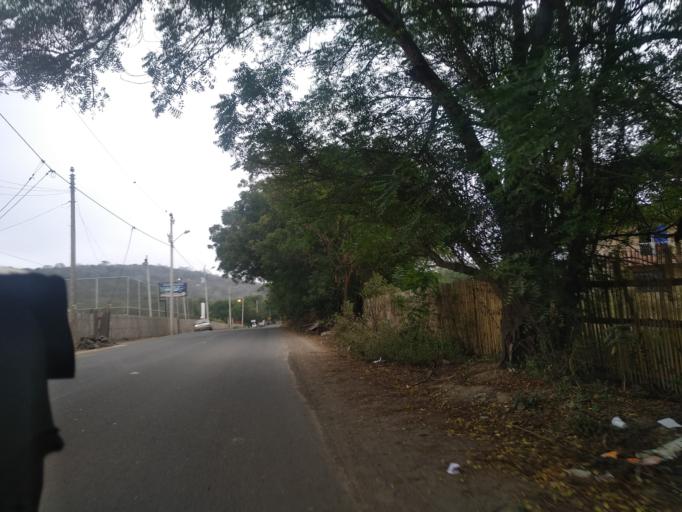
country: EC
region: Manabi
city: Montecristi
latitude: -1.0842
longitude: -80.6820
